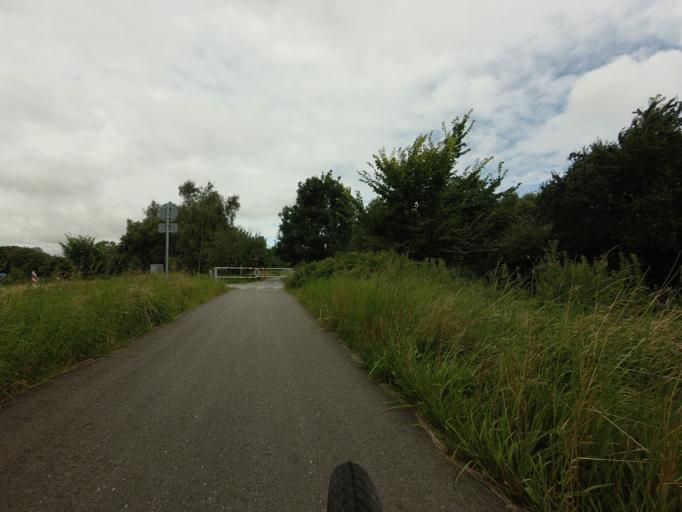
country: DK
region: Central Jutland
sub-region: Norddjurs Kommune
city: Auning
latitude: 56.3904
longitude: 10.4122
